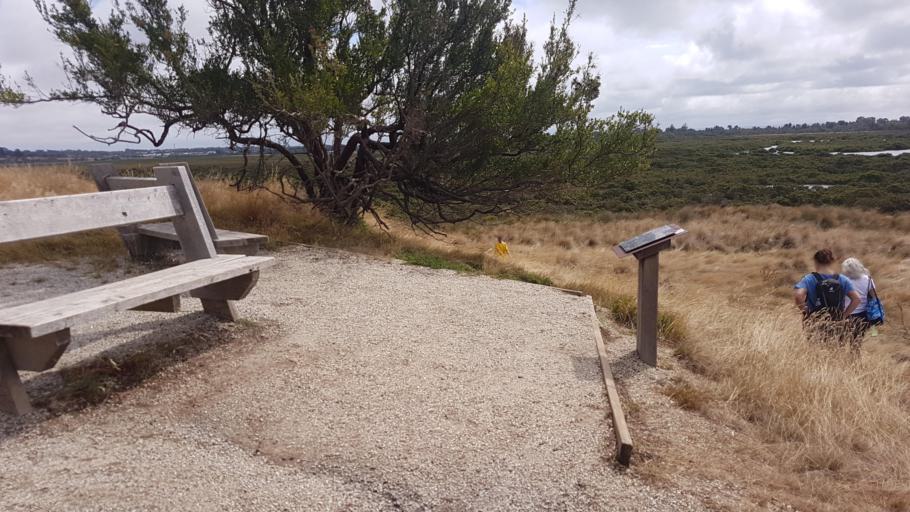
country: AU
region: Victoria
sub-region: Bass Coast
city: Cowes
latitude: -38.4576
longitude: 145.2902
